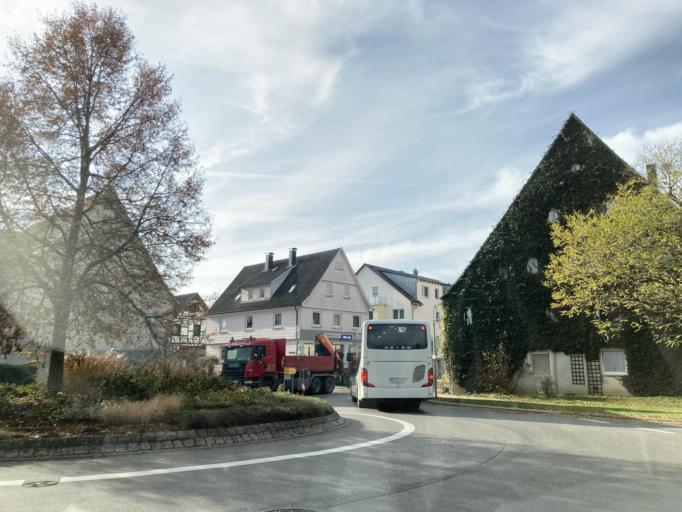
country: DE
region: Baden-Wuerttemberg
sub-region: Regierungsbezirk Stuttgart
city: Bondorf
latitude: 48.5209
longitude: 8.8375
